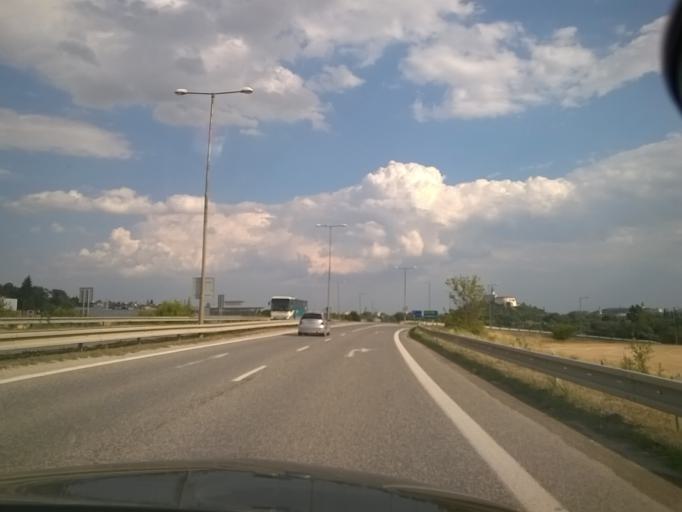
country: SK
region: Nitriansky
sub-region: Okres Nitra
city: Nitra
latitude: 48.3314
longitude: 18.0791
